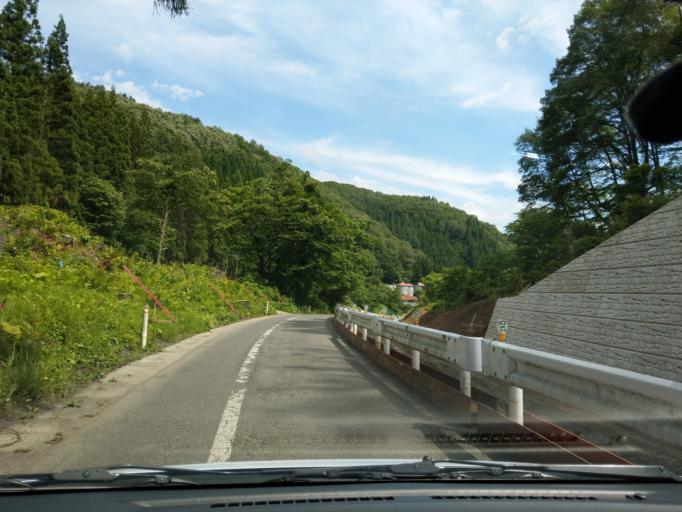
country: JP
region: Akita
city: Kakunodatemachi
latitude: 39.7226
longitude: 140.5825
